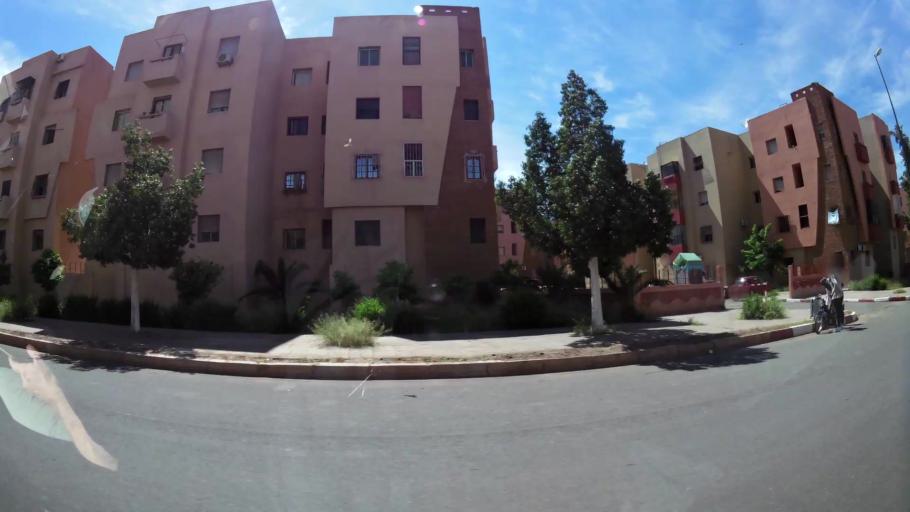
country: MA
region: Marrakech-Tensift-Al Haouz
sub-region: Marrakech
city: Marrakesh
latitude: 31.6348
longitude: -8.0775
